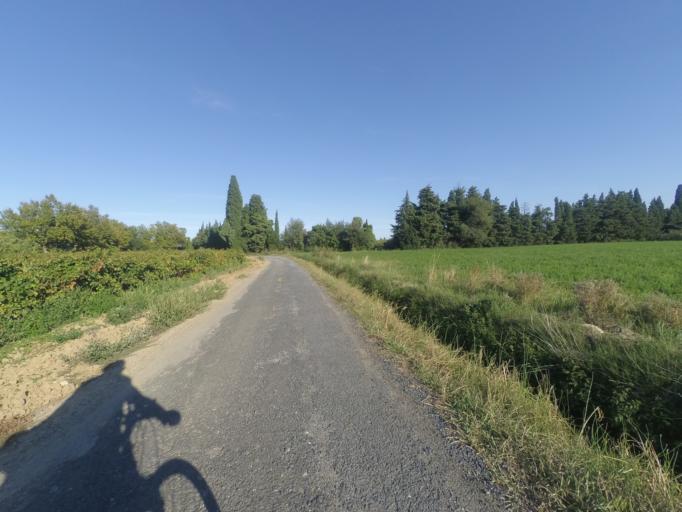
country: FR
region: Languedoc-Roussillon
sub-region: Departement des Pyrenees-Orientales
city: Corneilla-la-Riviere
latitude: 42.6984
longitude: 2.7202
